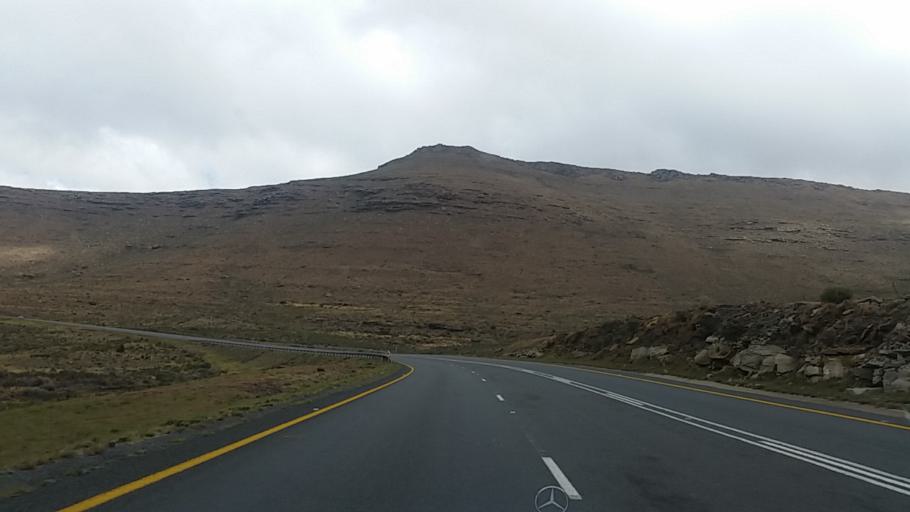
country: ZA
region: Eastern Cape
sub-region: Chris Hani District Municipality
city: Middelburg
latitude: -31.8180
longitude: 24.8623
